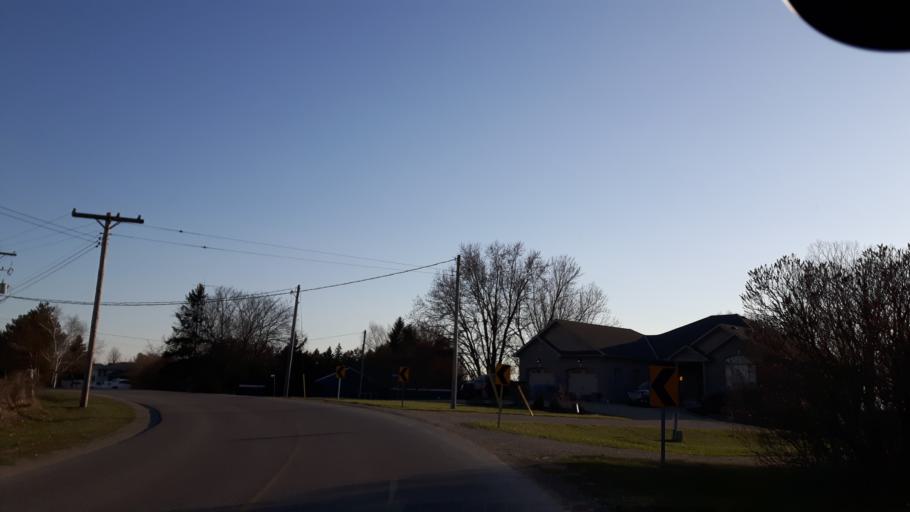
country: CA
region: Ontario
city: Goderich
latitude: 43.7205
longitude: -81.6850
